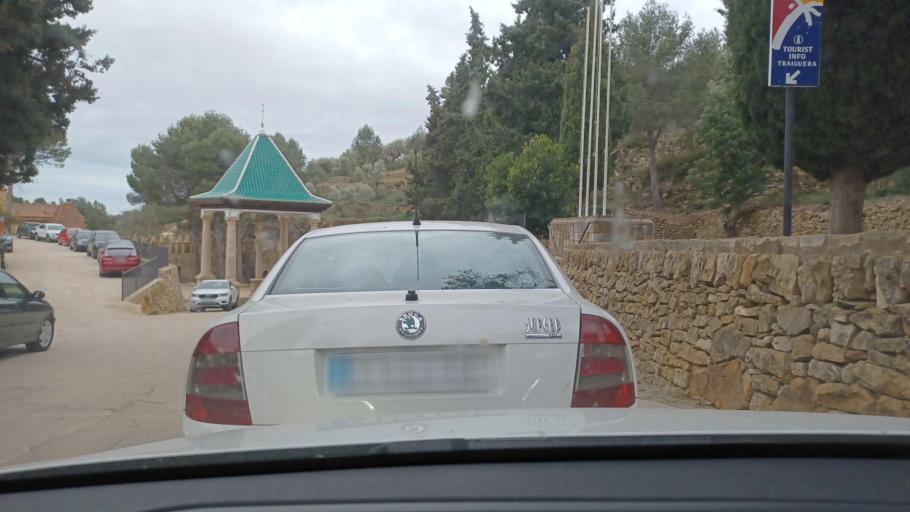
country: ES
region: Valencia
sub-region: Provincia de Castello
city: Traiguera
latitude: 40.5037
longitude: 0.2993
